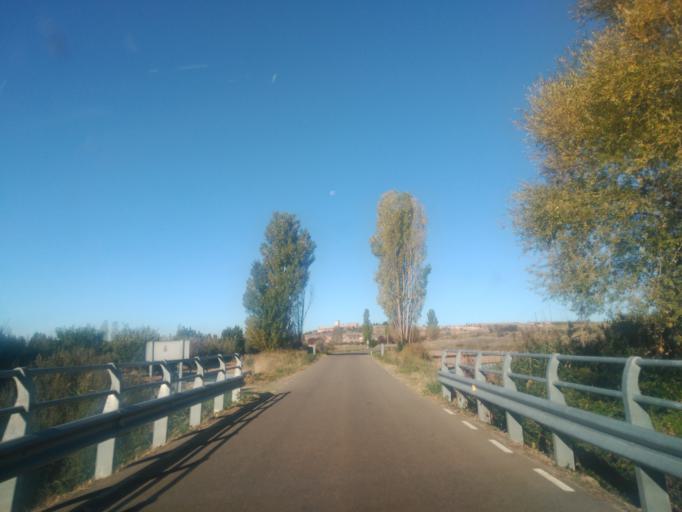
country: ES
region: Castille and Leon
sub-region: Provincia de Burgos
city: Penaranda de Duero
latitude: 41.6880
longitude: -3.4623
